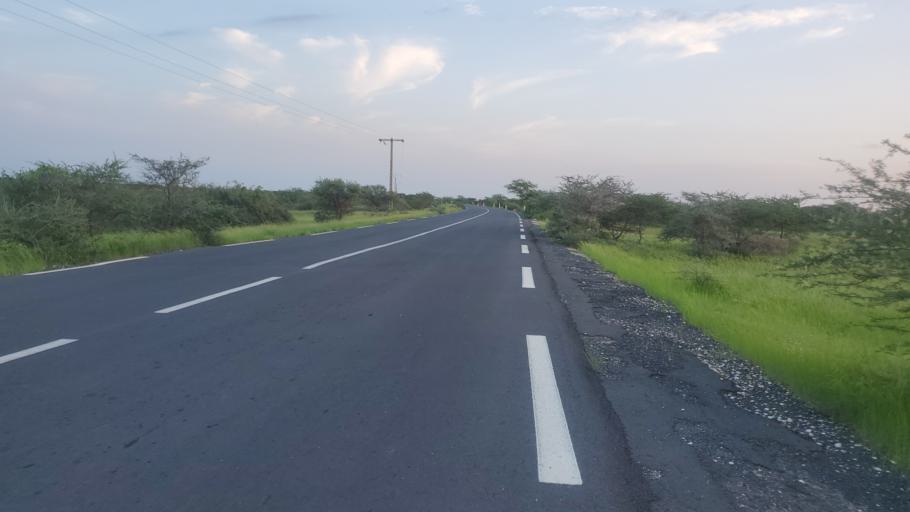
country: SN
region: Saint-Louis
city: Saint-Louis
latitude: 16.1228
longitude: -16.4140
